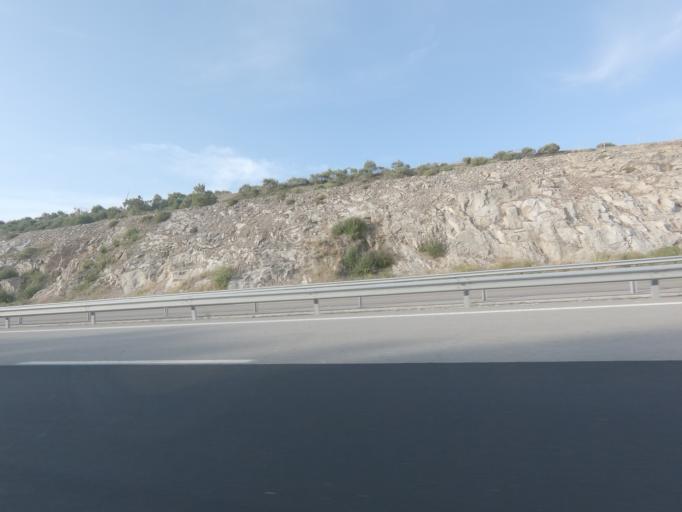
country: PT
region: Vila Real
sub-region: Vila Pouca de Aguiar
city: Vila Pouca de Aguiar
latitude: 41.4409
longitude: -7.6436
